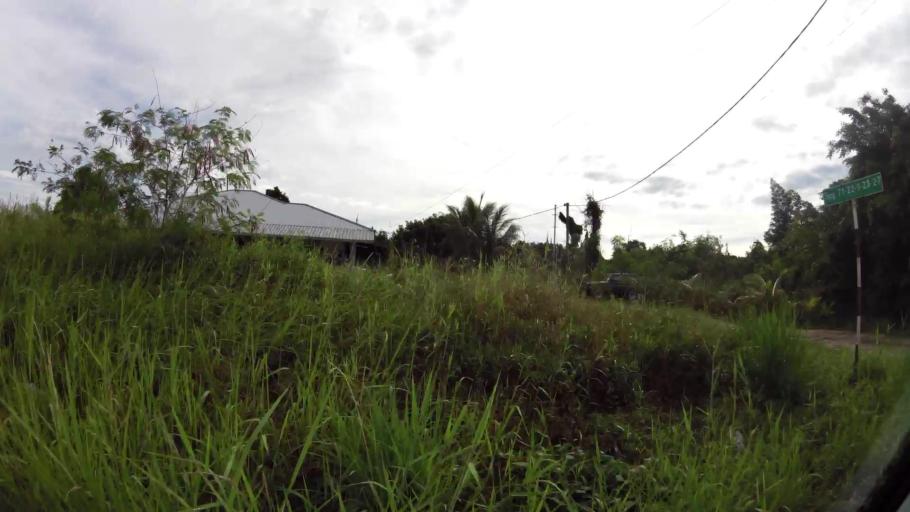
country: BN
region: Belait
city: Seria
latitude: 4.6136
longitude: 114.3628
